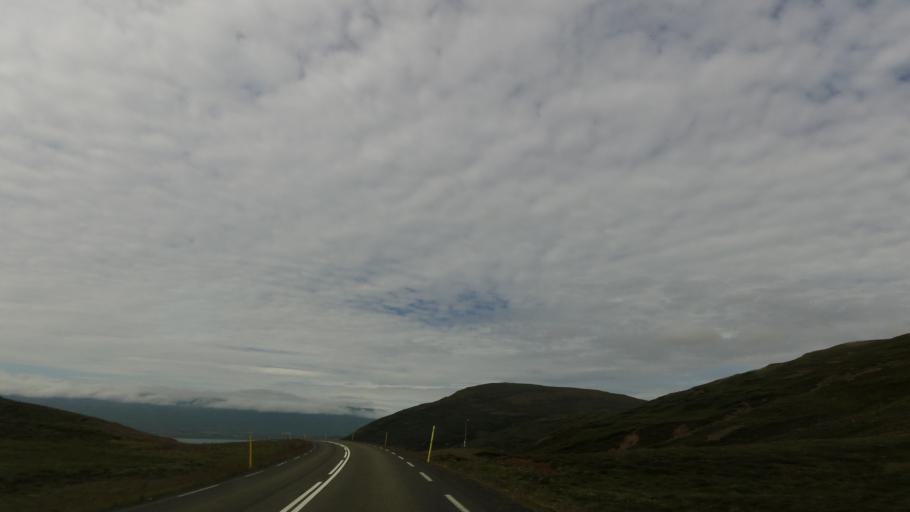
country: IS
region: Northeast
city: Akureyri
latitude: 65.8133
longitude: -17.9890
